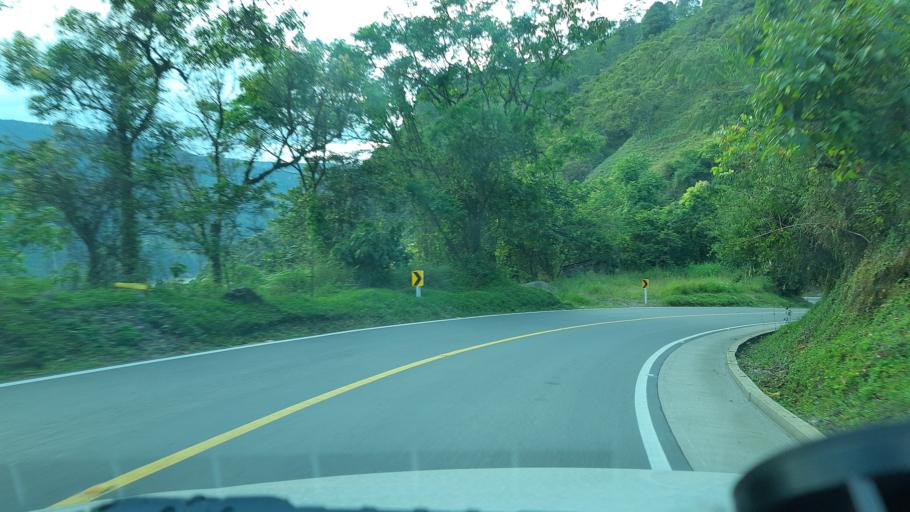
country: CO
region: Boyaca
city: Chivor
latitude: 4.9780
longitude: -73.3346
